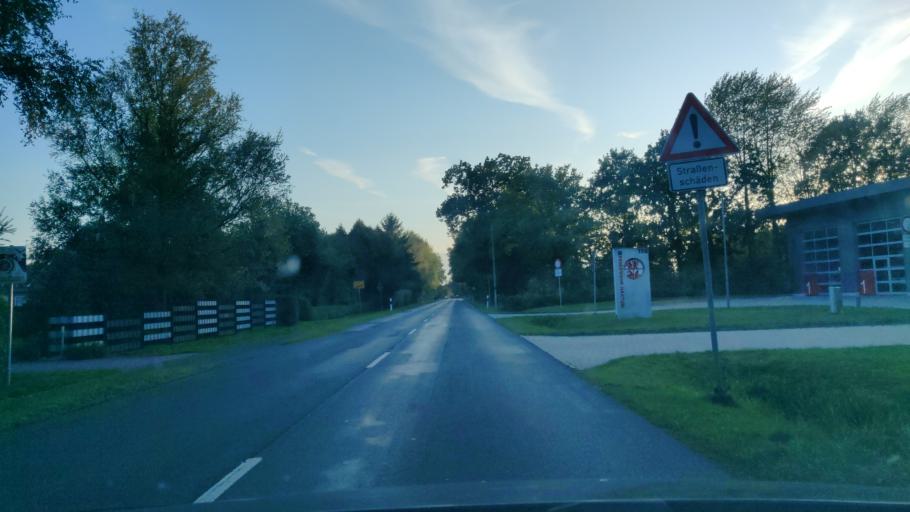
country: DE
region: Lower Saxony
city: Aurich
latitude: 53.4592
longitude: 7.4527
